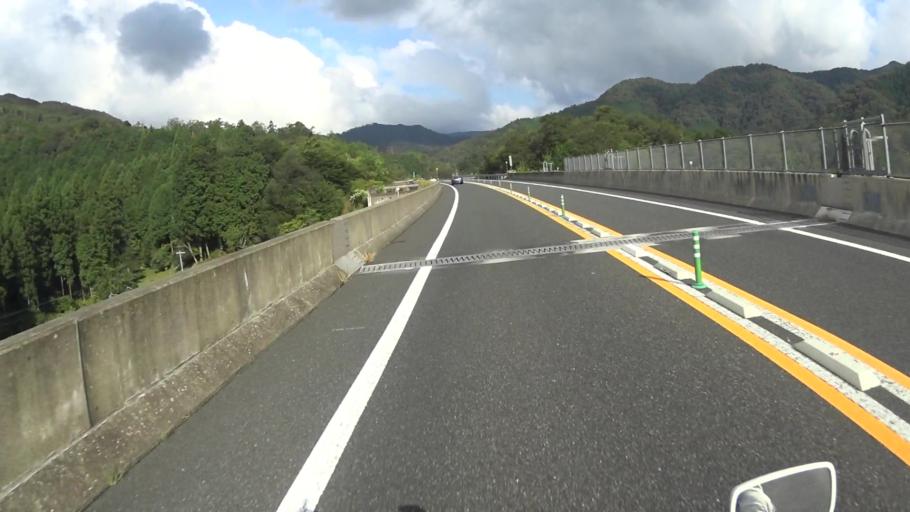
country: JP
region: Kyoto
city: Miyazu
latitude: 35.4487
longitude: 135.1842
